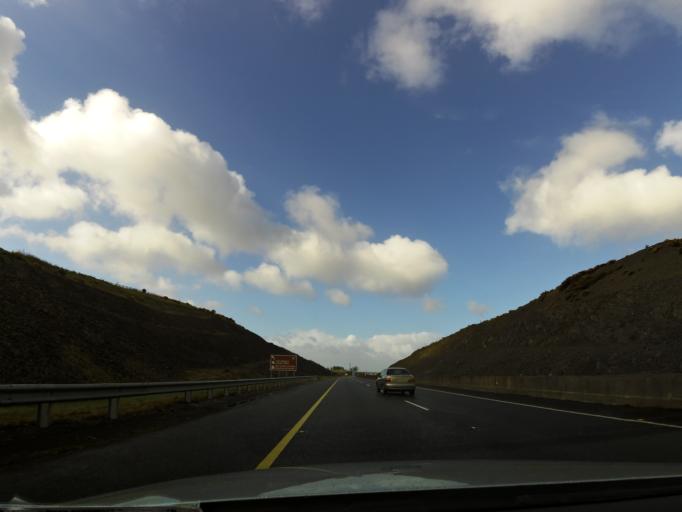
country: IE
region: Munster
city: Ballina
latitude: 52.7707
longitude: -8.3849
